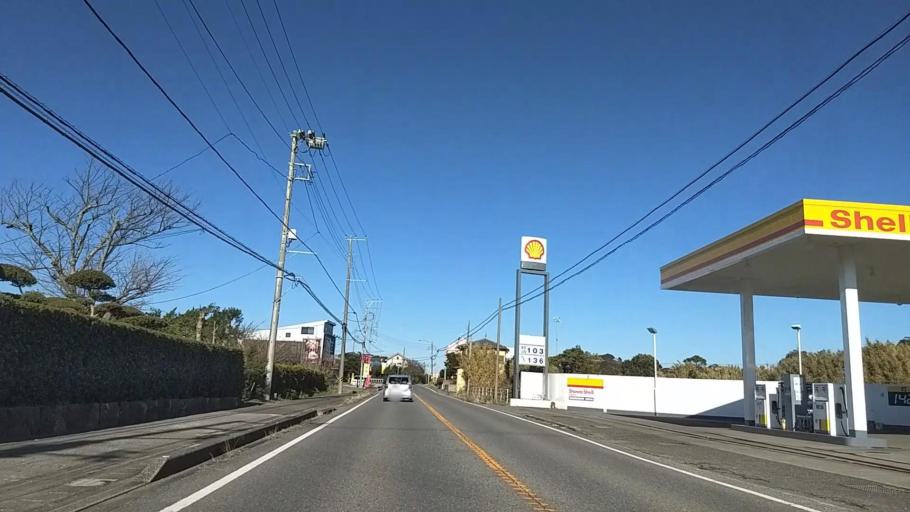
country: JP
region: Chiba
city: Ohara
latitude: 35.3171
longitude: 140.4026
